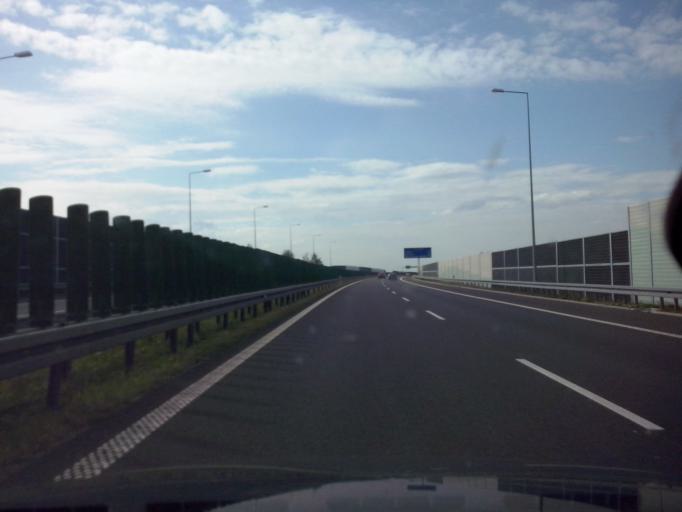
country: PL
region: Lesser Poland Voivodeship
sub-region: Powiat tarnowski
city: Lisia Gora
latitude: 50.0545
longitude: 21.0082
